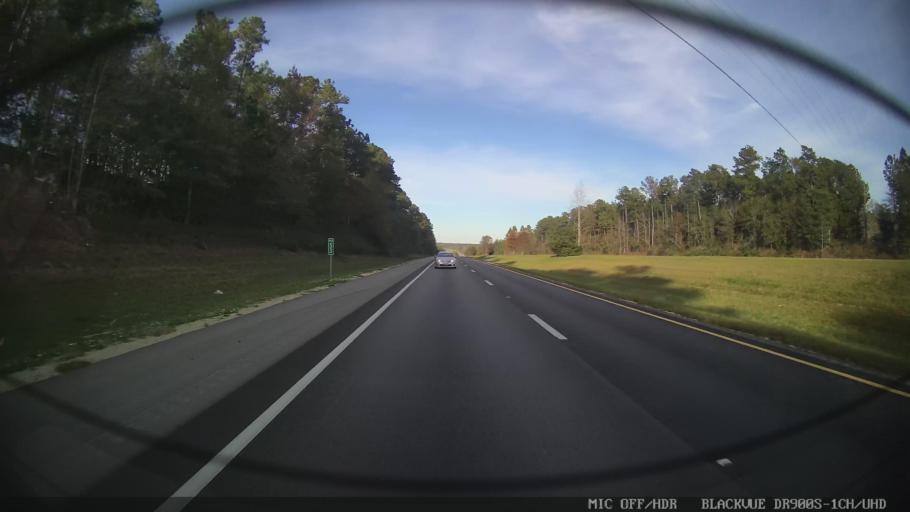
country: US
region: Mississippi
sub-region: Lamar County
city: Purvis
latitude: 31.1586
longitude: -89.3583
